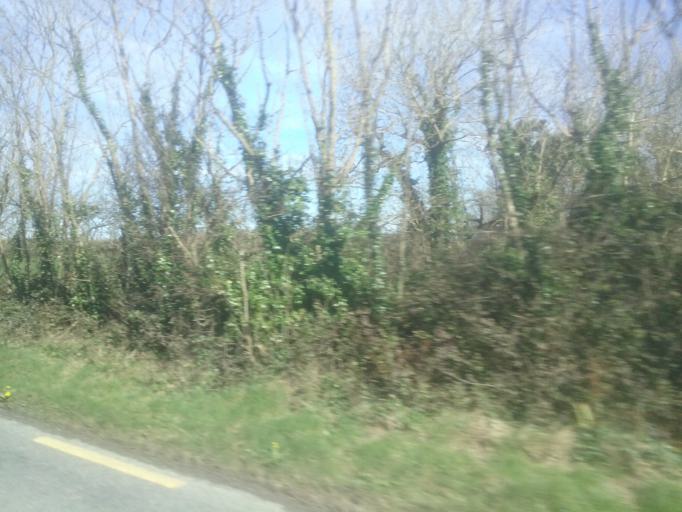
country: IE
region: Munster
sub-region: An Clar
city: Kilrush
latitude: 52.6162
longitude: -9.4548
